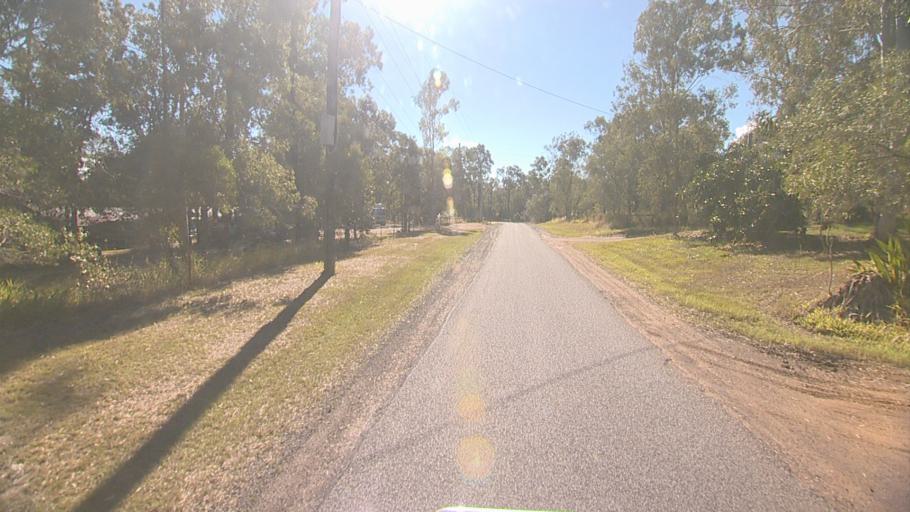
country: AU
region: Queensland
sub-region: Logan
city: Chambers Flat
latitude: -27.8056
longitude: 153.0789
